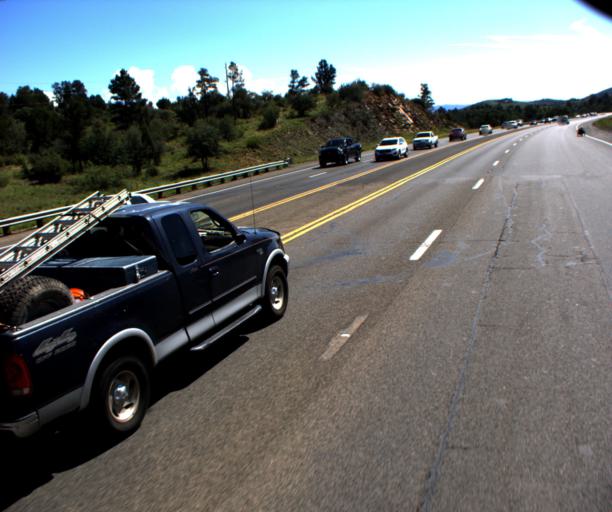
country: US
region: Arizona
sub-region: Yavapai County
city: Prescott
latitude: 34.5488
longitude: -112.3962
